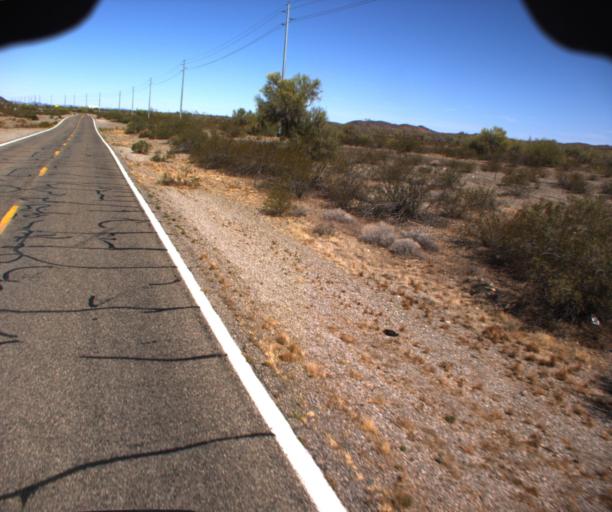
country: US
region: Arizona
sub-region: La Paz County
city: Salome
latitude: 33.7401
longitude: -113.7404
